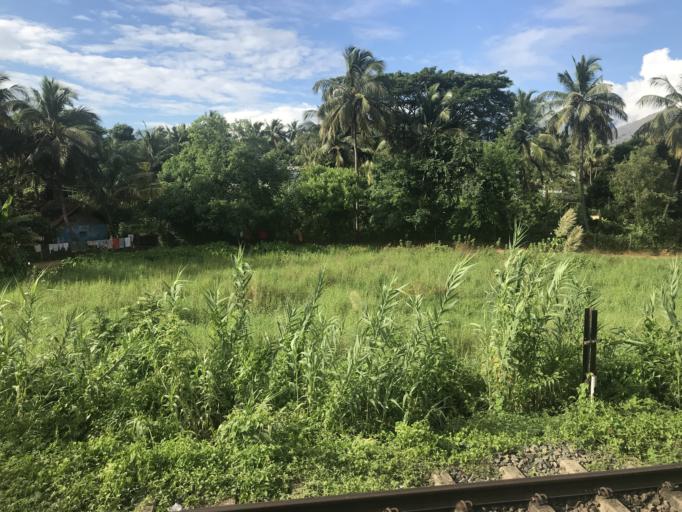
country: IN
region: Kerala
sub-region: Palakkad district
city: Palakkad
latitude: 10.8044
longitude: 76.6466
